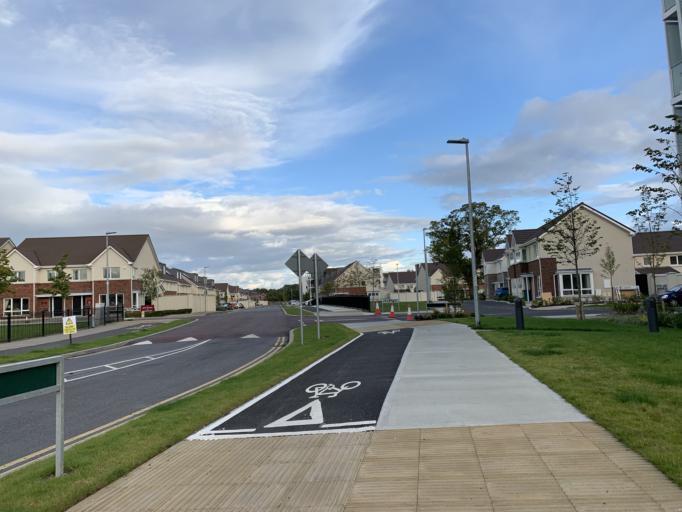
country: IE
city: Palmerstown
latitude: 53.3693
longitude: -6.3858
